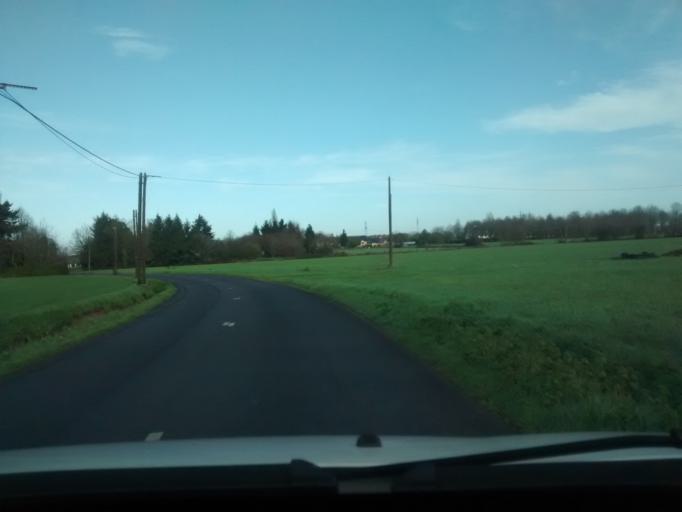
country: FR
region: Brittany
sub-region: Departement d'Ille-et-Vilaine
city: Montgermont
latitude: 48.1344
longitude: -1.7127
